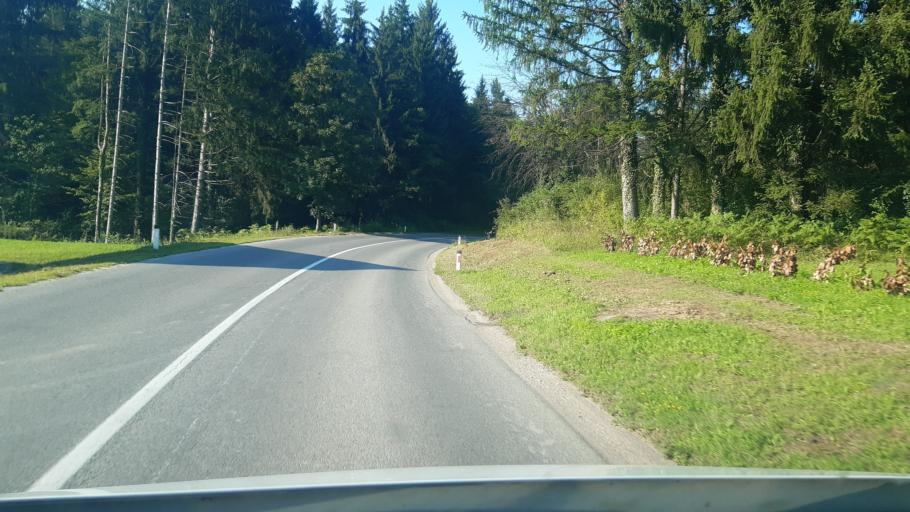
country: SI
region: Crnomelj
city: Crnomelj
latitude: 45.5557
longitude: 15.1662
